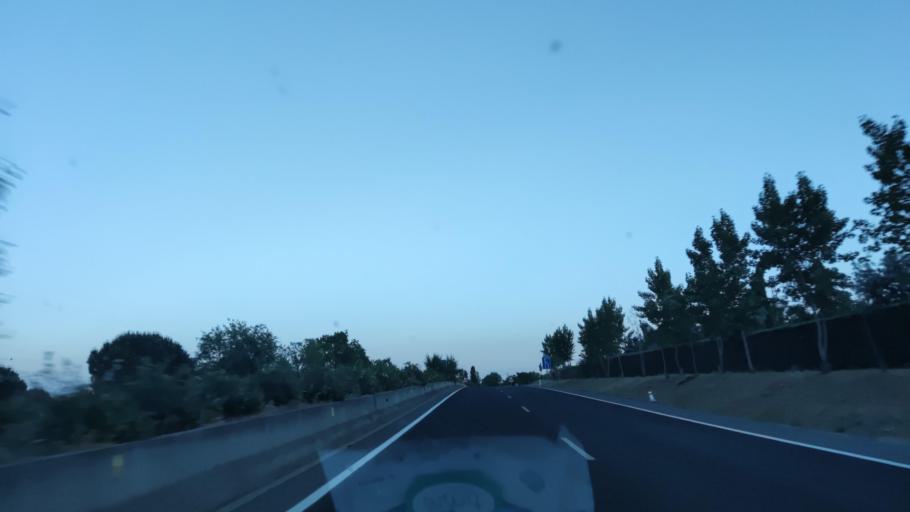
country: ES
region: Madrid
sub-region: Provincia de Madrid
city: San Sebastian de los Reyes
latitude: 40.5186
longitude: -3.5924
